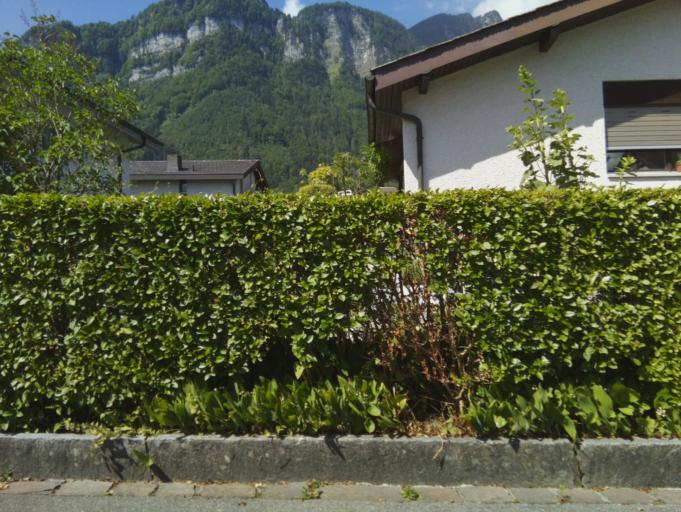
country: CH
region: Glarus
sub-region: Glarus
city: Oberurnen
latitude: 47.1150
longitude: 9.0640
